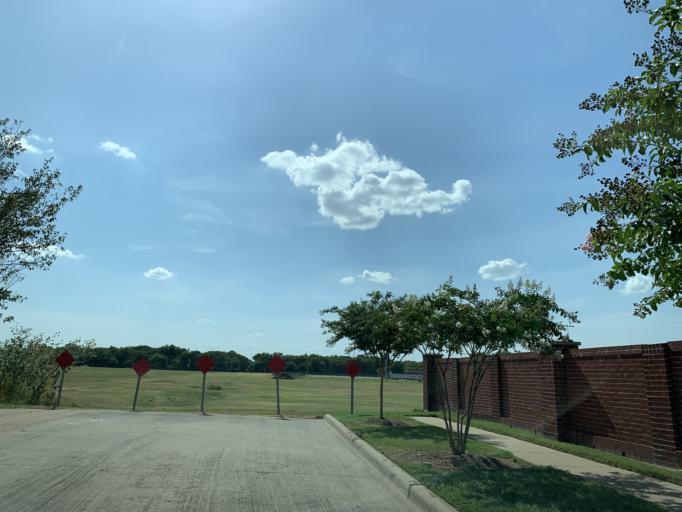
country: US
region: Texas
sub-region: Dallas County
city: Cedar Hill
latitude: 32.6490
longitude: -97.0103
